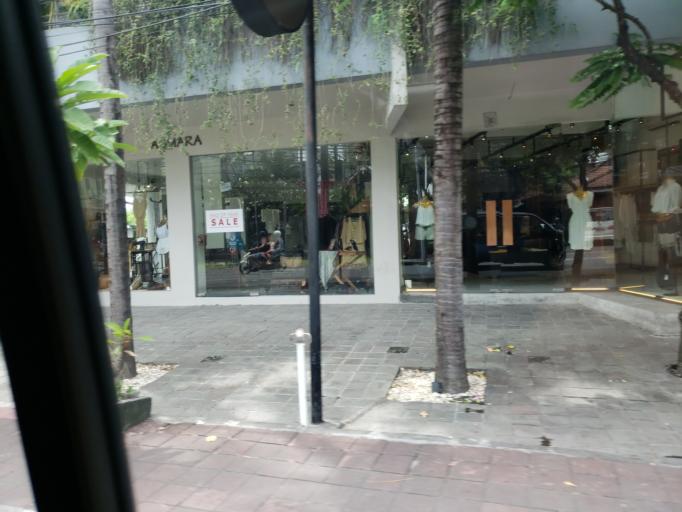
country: ID
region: Bali
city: Kuta
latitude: -8.6784
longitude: 115.1536
